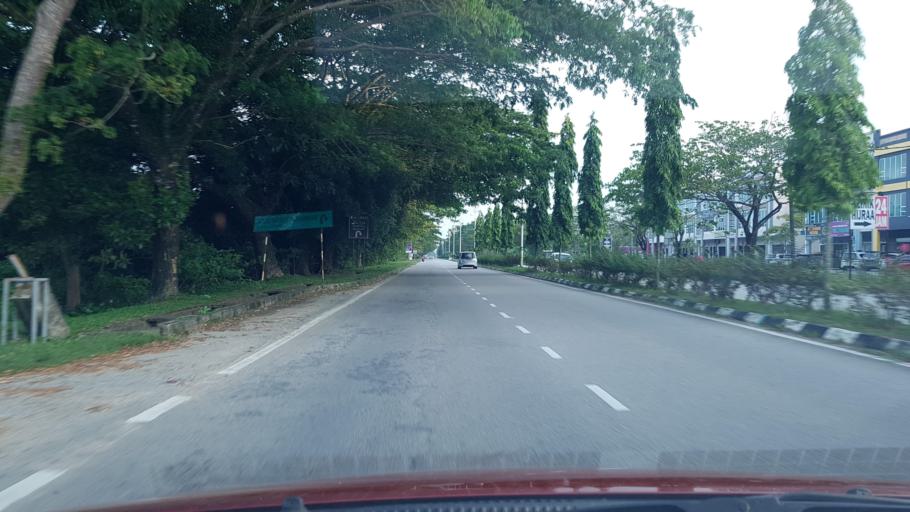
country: MY
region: Terengganu
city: Kuala Terengganu
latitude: 5.3491
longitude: 103.1029
